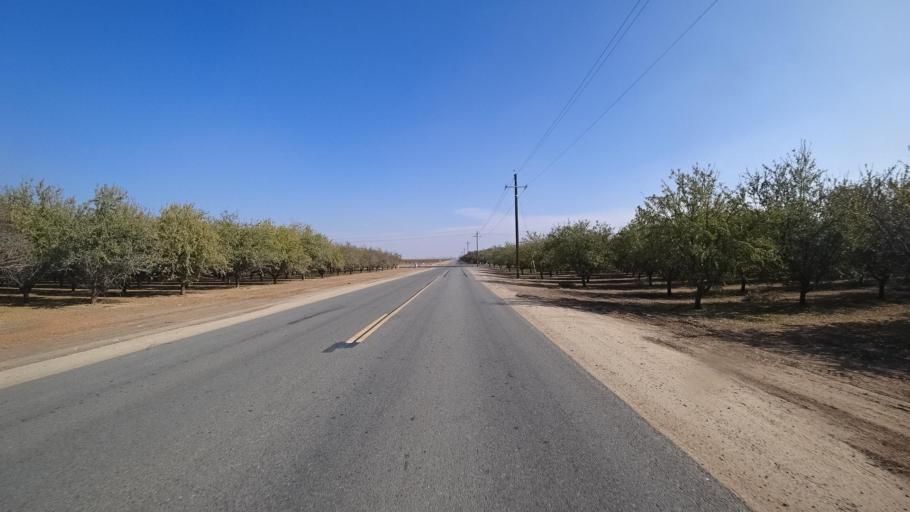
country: US
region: California
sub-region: Kern County
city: Shafter
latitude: 35.5295
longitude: -119.1529
